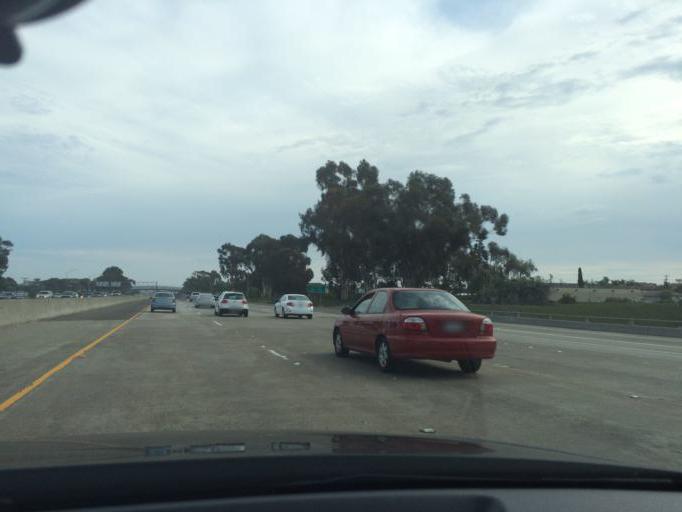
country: US
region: California
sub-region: San Diego County
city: San Diego
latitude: 32.7920
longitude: -117.1590
